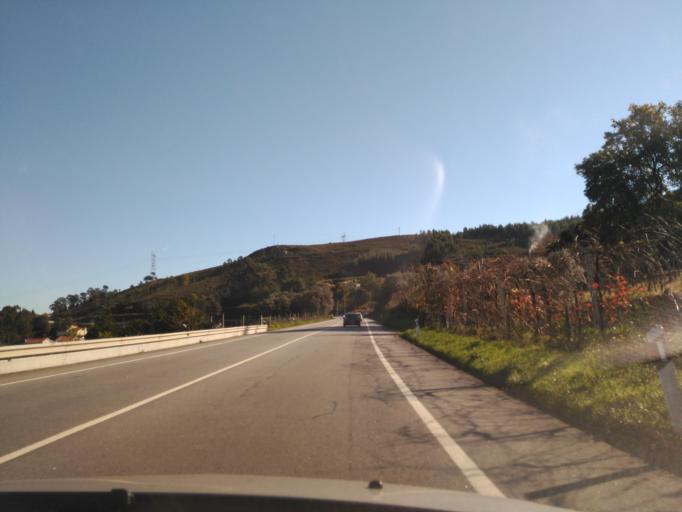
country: PT
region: Braga
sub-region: Amares
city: Amares
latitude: 41.5873
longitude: -8.3353
